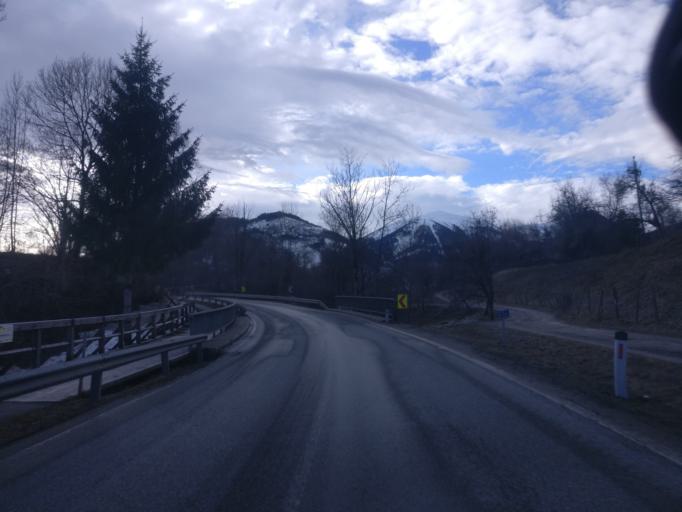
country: AT
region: Styria
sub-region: Politischer Bezirk Liezen
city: Hall bei Admont
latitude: 47.5921
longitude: 14.4724
